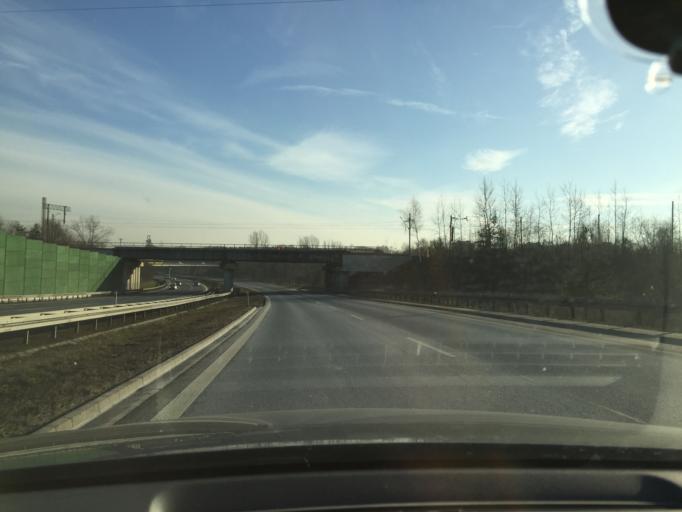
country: PL
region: Silesian Voivodeship
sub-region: Katowice
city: Murcki
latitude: 50.2327
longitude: 19.0639
